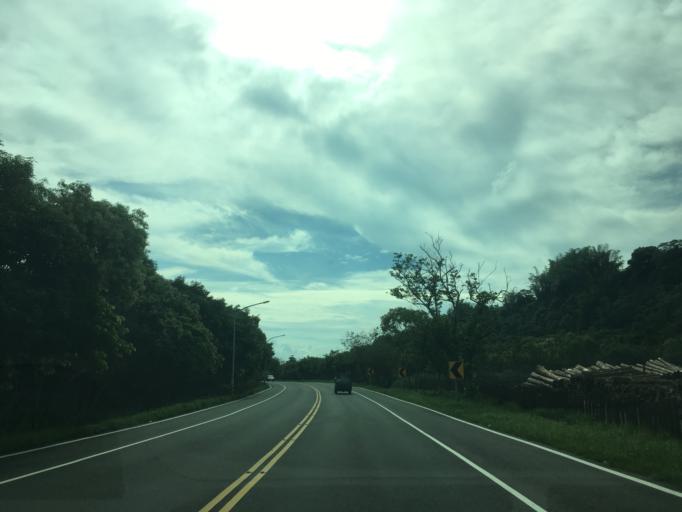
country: TW
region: Taiwan
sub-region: Chiayi
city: Jiayi Shi
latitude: 23.4523
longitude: 120.5650
